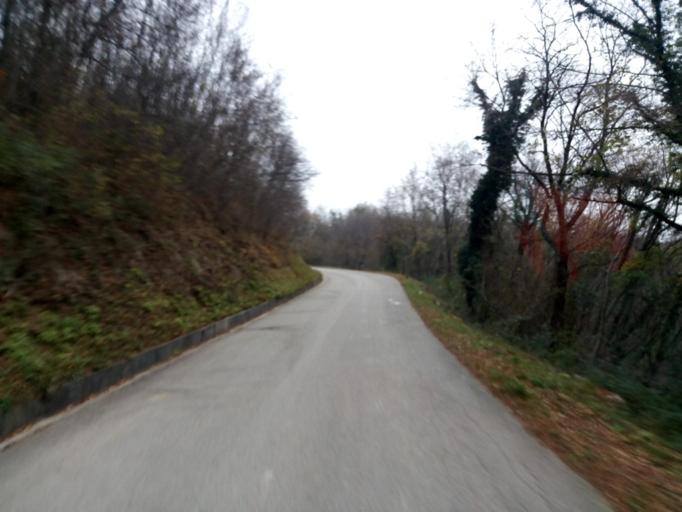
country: IT
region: Friuli Venezia Giulia
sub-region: Provincia di Udine
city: Merso di Sopra
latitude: 46.1250
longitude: 13.5185
